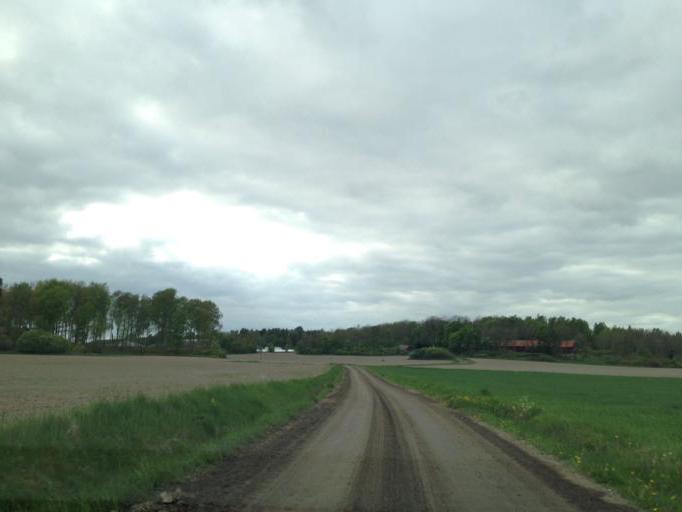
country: SE
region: Soedermanland
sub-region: Eskilstuna Kommun
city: Kvicksund
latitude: 59.4344
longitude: 16.3057
